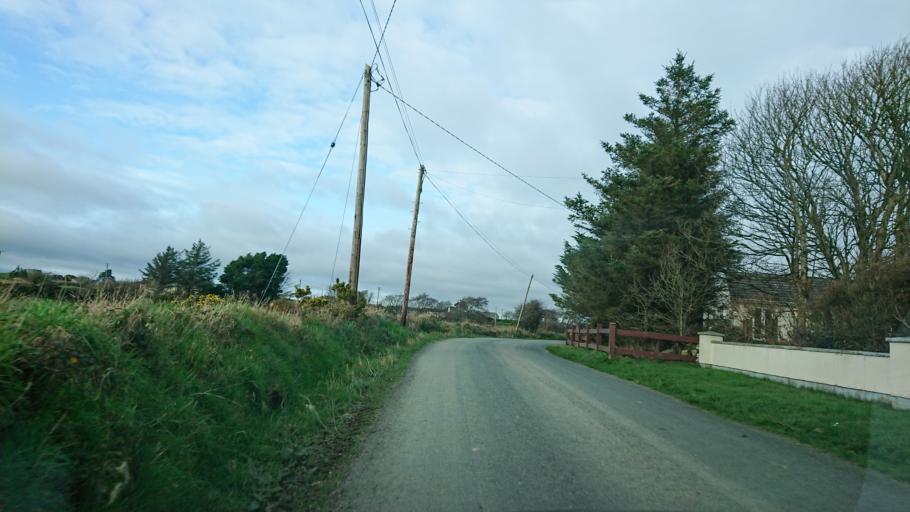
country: IE
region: Munster
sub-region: Waterford
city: Portlaw
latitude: 52.1486
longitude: -7.3086
